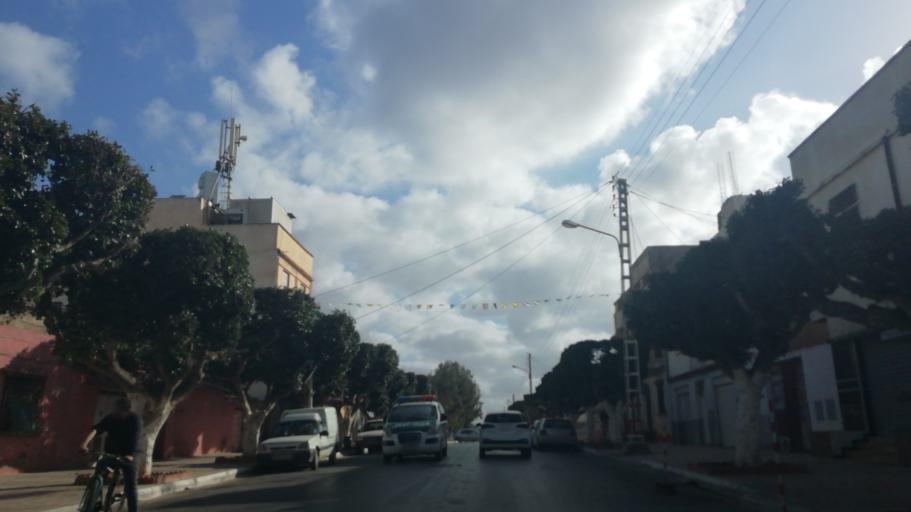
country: DZ
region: Relizane
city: Mazouna
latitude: 36.2544
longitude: 0.5763
